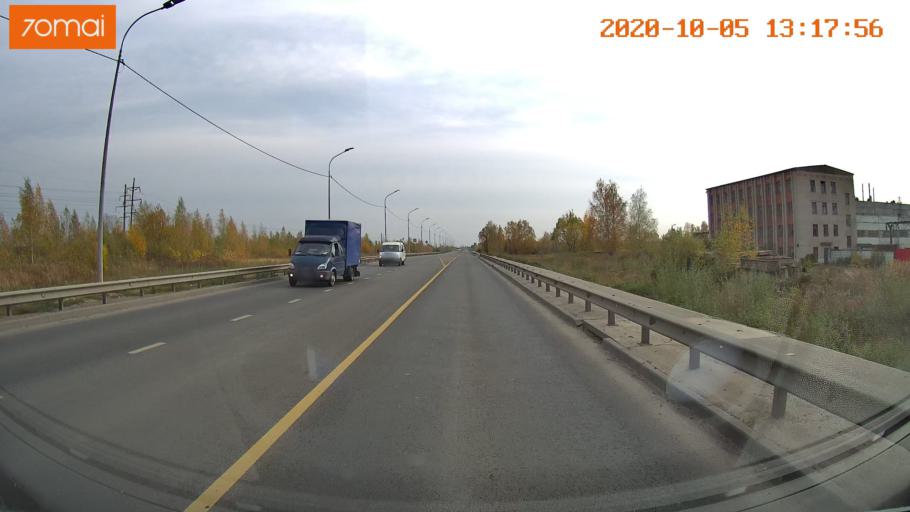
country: RU
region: Ivanovo
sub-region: Gorod Ivanovo
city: Ivanovo
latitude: 56.9818
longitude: 40.9149
